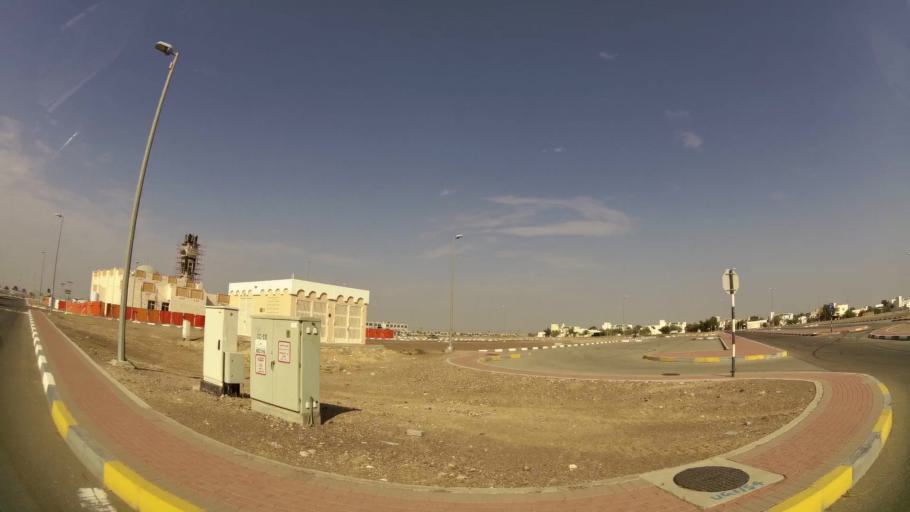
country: AE
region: Abu Dhabi
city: Al Ain
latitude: 24.0890
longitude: 55.8651
